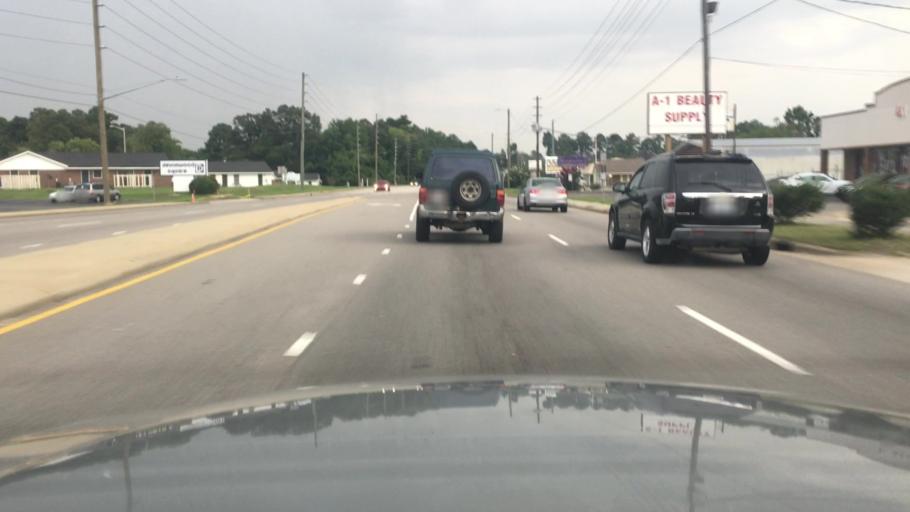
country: US
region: North Carolina
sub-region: Cumberland County
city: Fort Bragg
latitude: 35.0820
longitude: -79.0102
